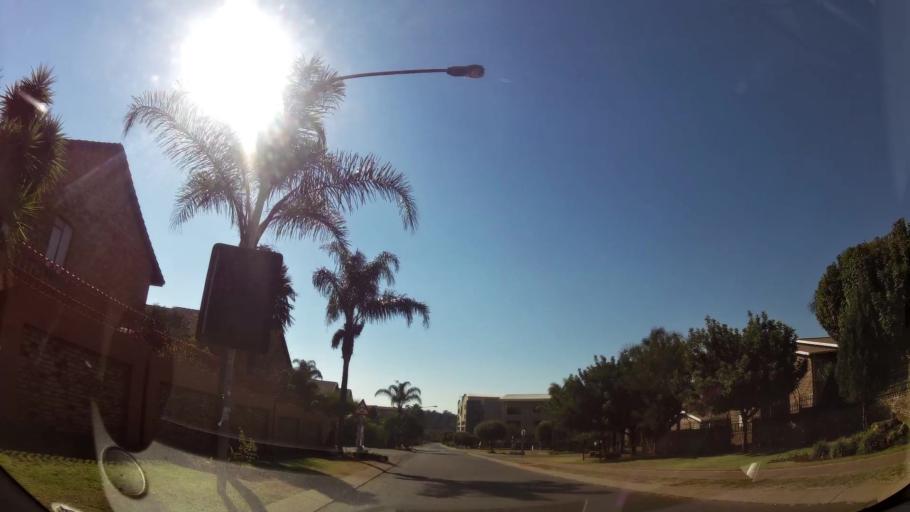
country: ZA
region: Gauteng
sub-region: City of Tshwane Metropolitan Municipality
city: Centurion
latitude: -25.8528
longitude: 28.1807
